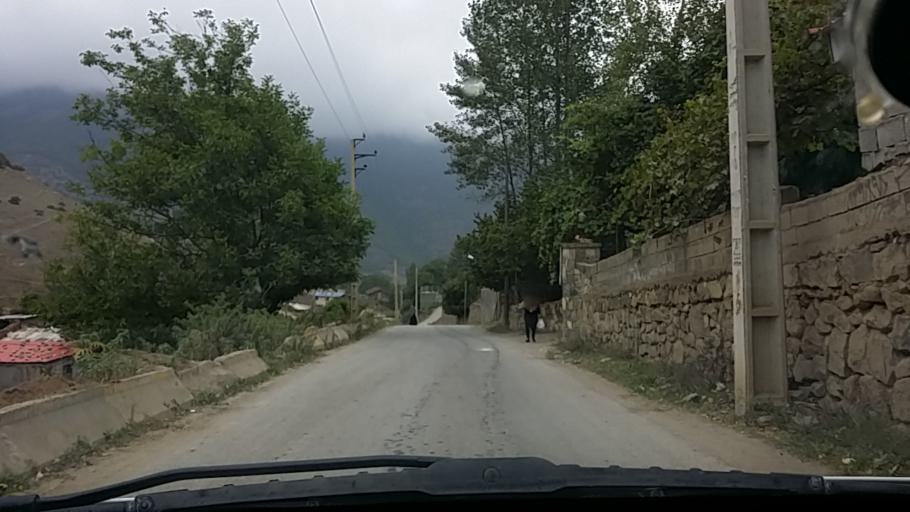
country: IR
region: Mazandaran
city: `Abbasabad
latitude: 36.4791
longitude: 51.1386
